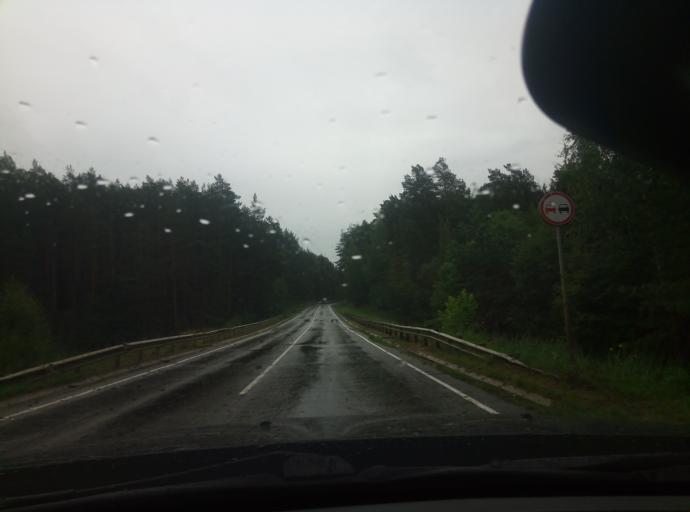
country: RU
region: Kaluga
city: Vysokinichi
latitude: 54.9251
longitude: 36.8889
